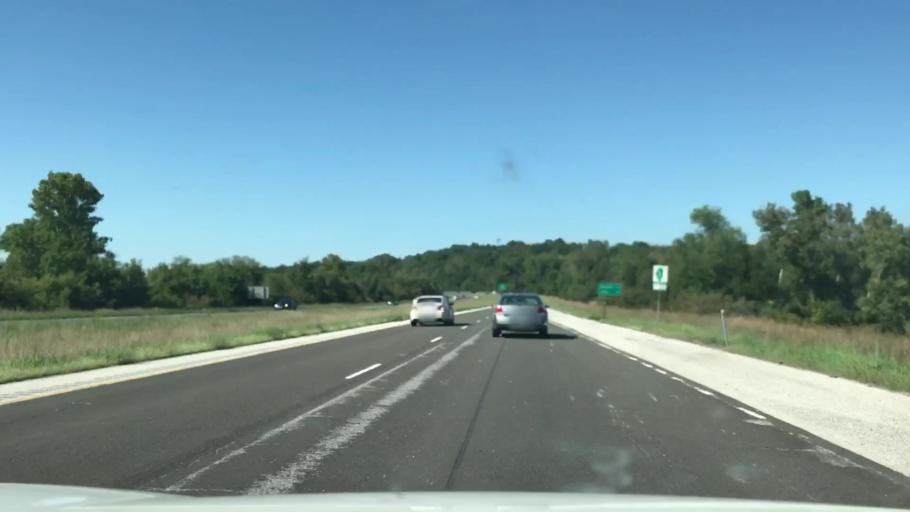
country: US
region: Illinois
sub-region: Madison County
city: South Roxana
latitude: 38.8350
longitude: -90.0435
